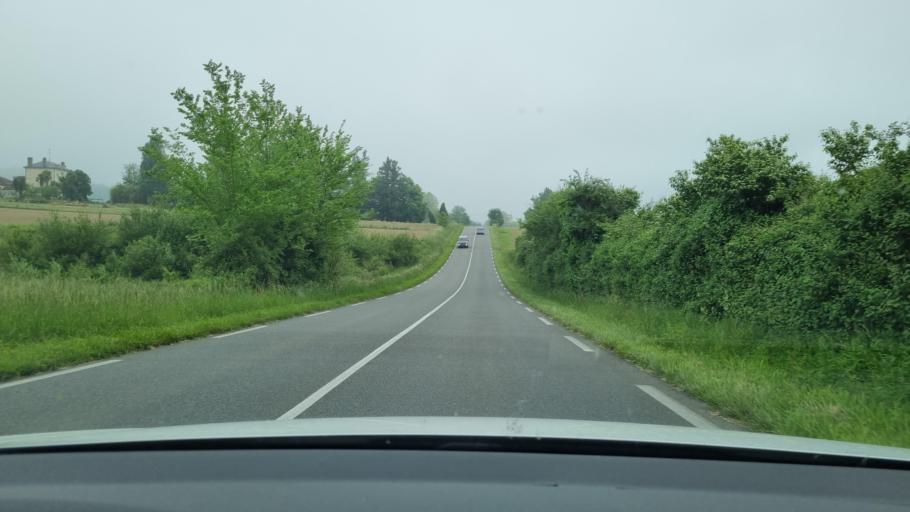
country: FR
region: Aquitaine
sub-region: Departement des Pyrenees-Atlantiques
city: Orthez
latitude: 43.4956
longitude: -0.7586
